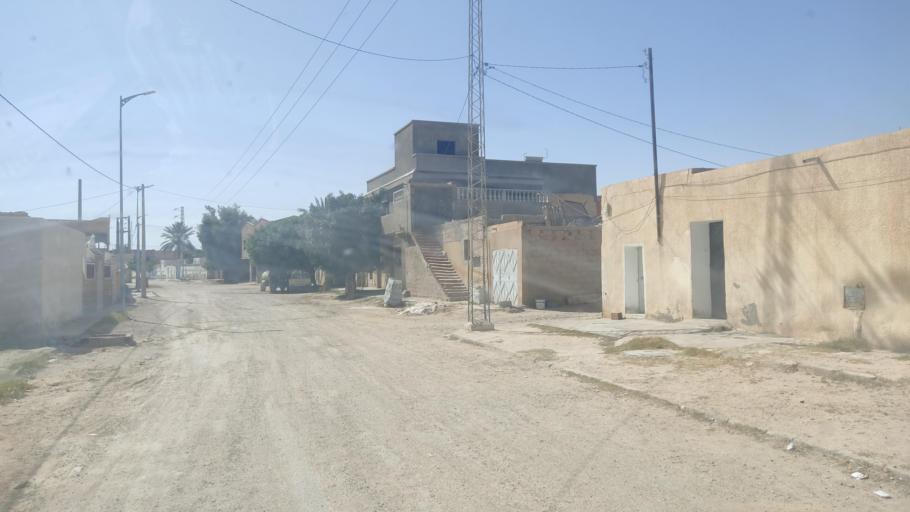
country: TN
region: Gafsa
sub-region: Gafsa Municipality
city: Gafsa
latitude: 34.3363
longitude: 8.9222
